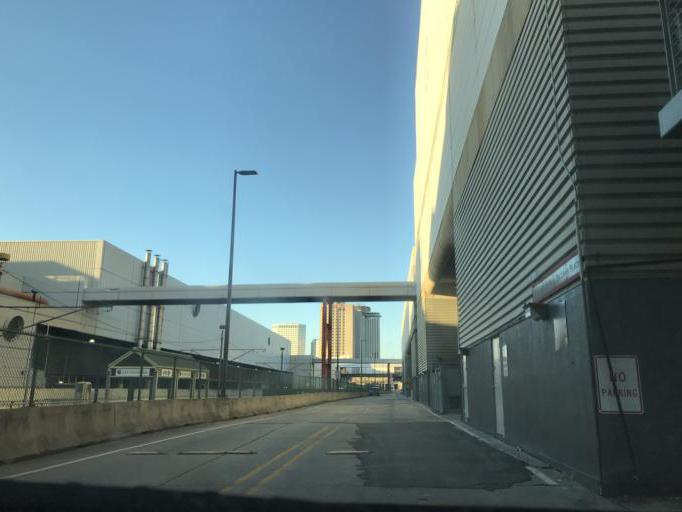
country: US
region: Louisiana
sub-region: Orleans Parish
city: New Orleans
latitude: 29.9413
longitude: -90.0620
